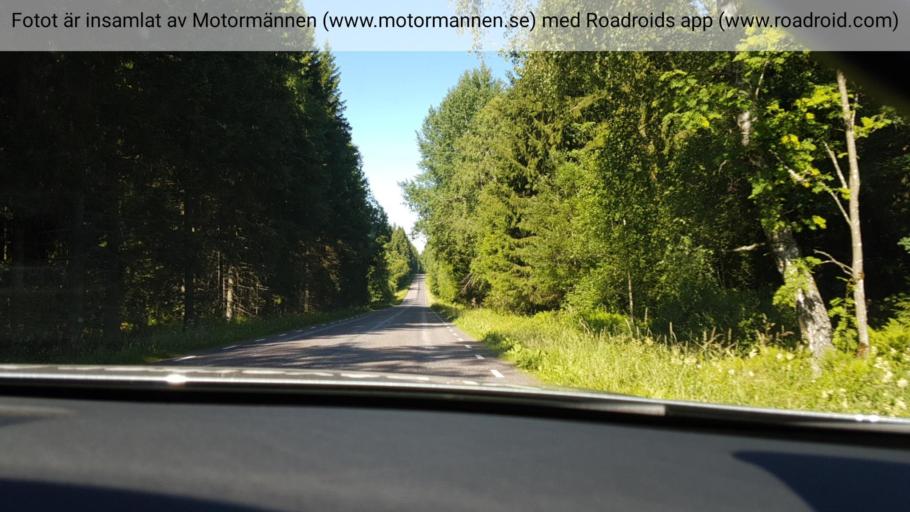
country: SE
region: Vaestra Goetaland
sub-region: Ulricehamns Kommun
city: Ulricehamn
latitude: 57.8401
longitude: 13.3649
